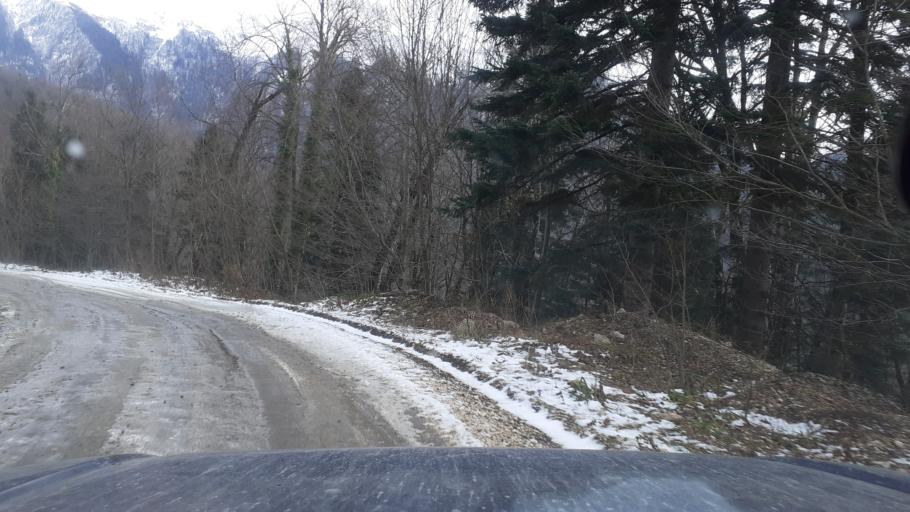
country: RU
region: Krasnodarskiy
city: Neftegorsk
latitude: 44.0742
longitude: 39.7821
